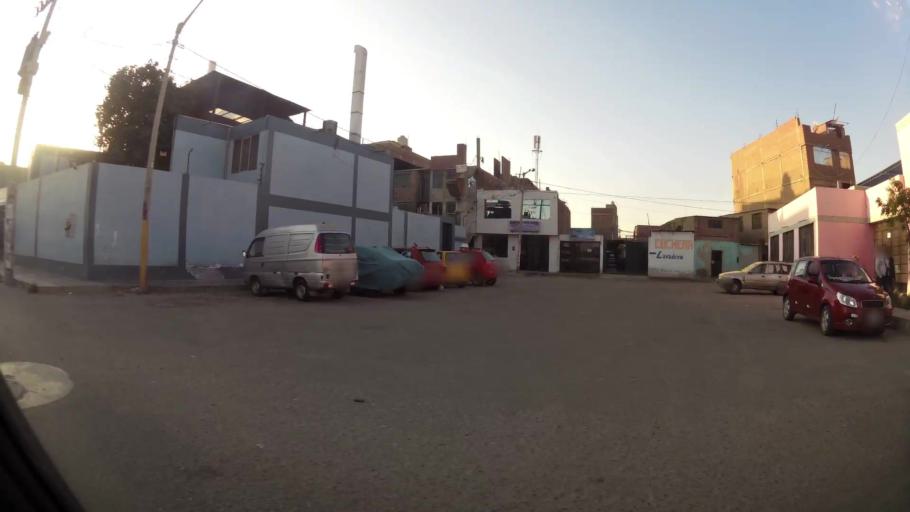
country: PE
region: Lambayeque
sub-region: Provincia de Chiclayo
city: Santa Rosa
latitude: -6.7733
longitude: -79.8333
